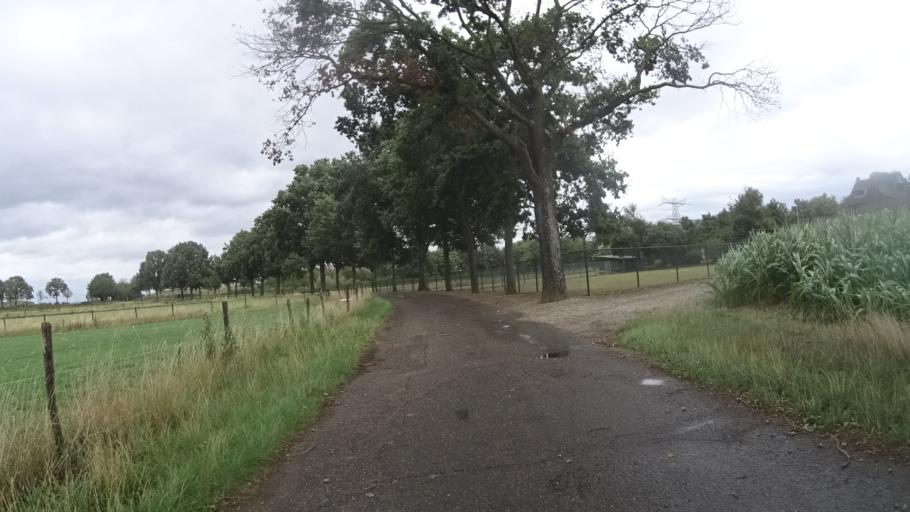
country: NL
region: Limburg
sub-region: Gemeente Sittard-Geleen
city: Born
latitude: 51.0441
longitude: 5.7862
